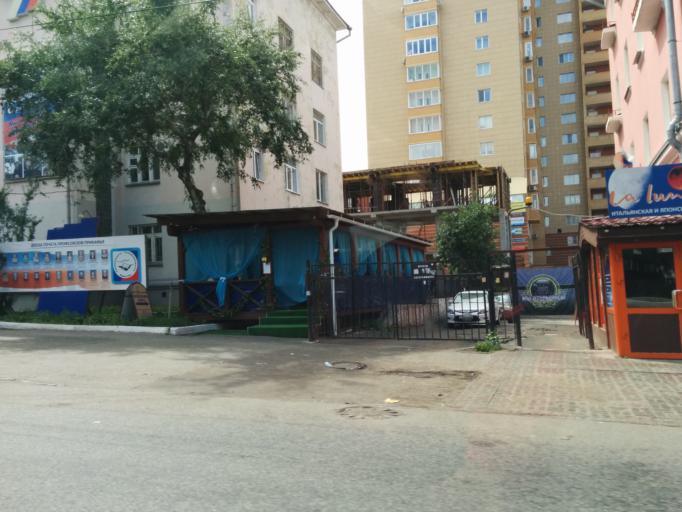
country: RU
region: Perm
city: Perm
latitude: 58.0059
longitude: 56.2436
